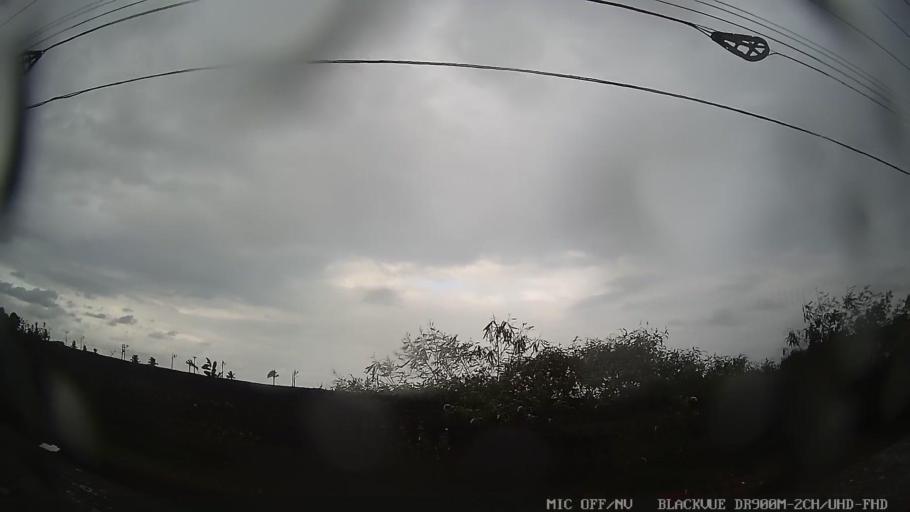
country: BR
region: Sao Paulo
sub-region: Mongagua
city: Mongagua
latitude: -24.1343
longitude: -46.6973
